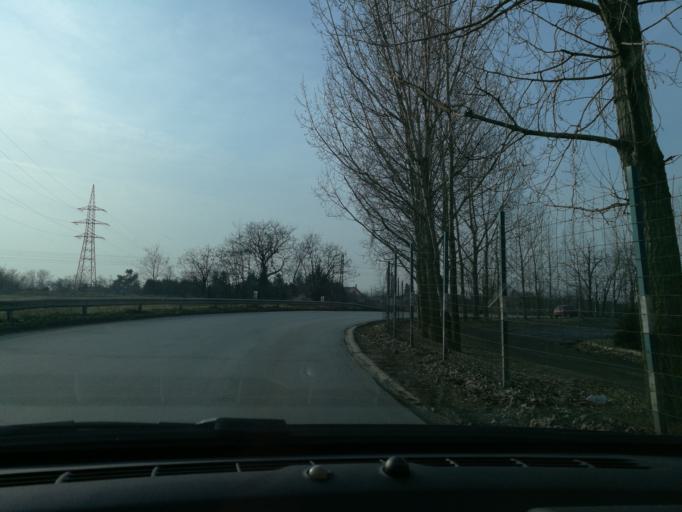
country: HU
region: Szabolcs-Szatmar-Bereg
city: Nyiregyhaza
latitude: 47.9327
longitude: 21.7157
